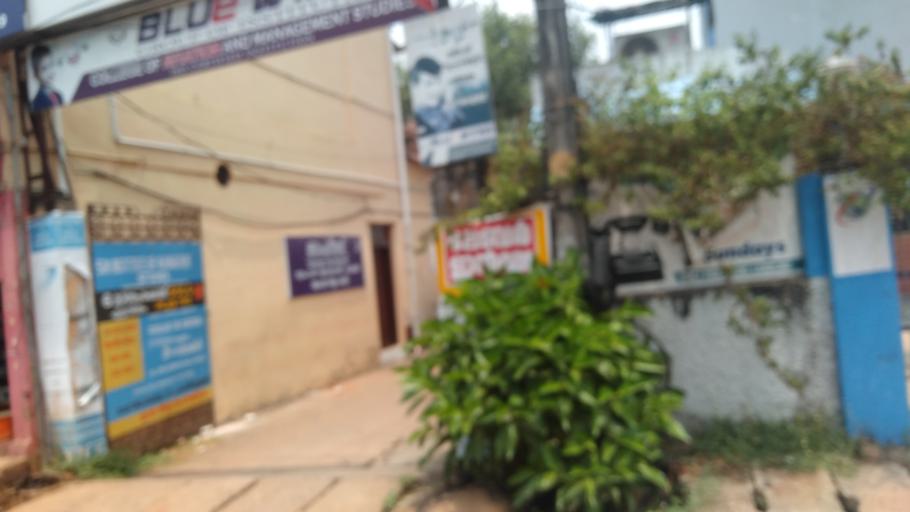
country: IN
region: Kerala
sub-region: Alappuzha
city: Alleppey
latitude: 9.4955
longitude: 76.3396
